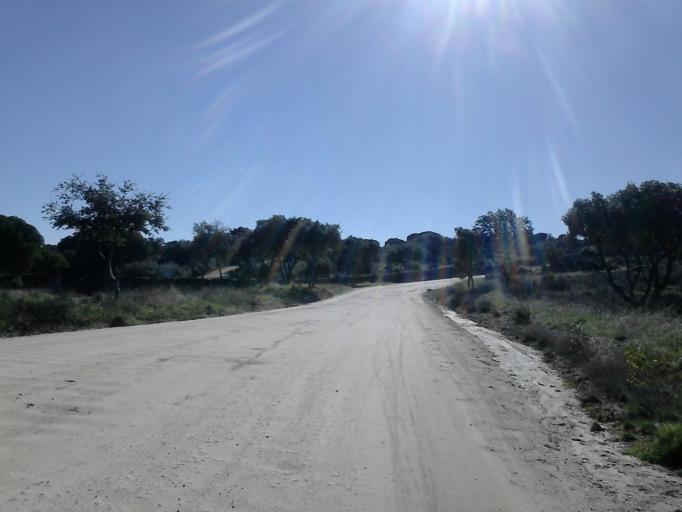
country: ES
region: Madrid
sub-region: Provincia de Madrid
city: Galapagar
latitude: 40.5592
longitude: -3.9813
